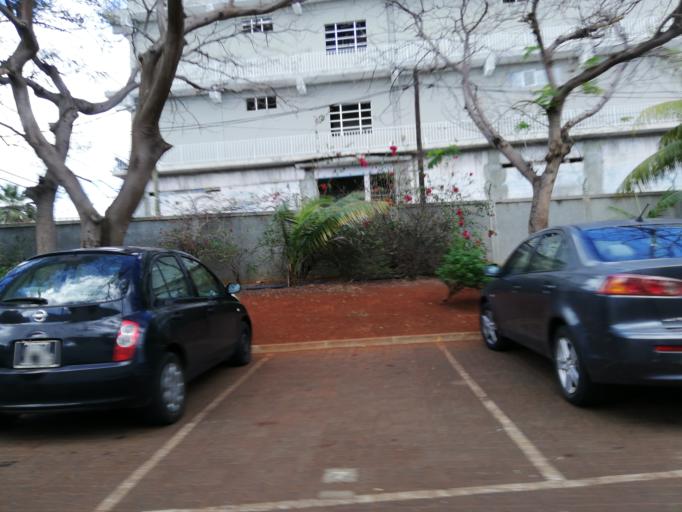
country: MU
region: Black River
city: Petite Riviere
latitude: -20.1902
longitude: 57.4658
